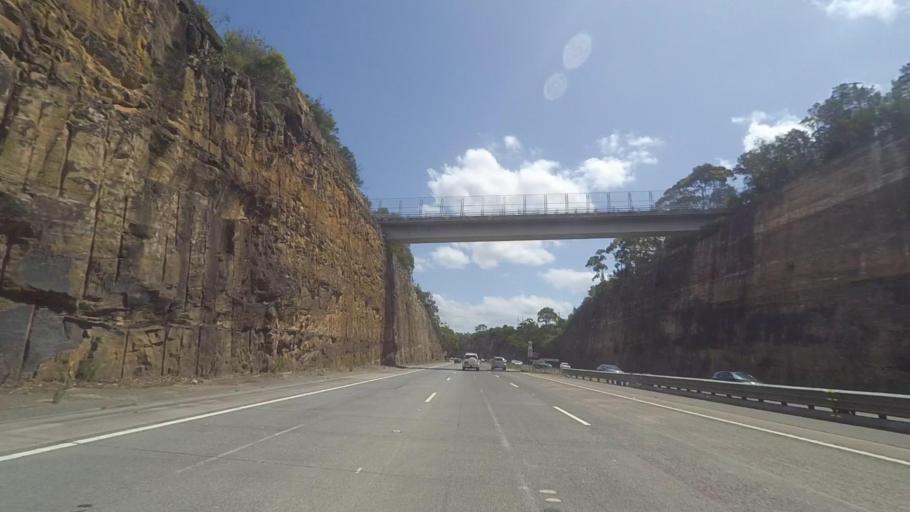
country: AU
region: New South Wales
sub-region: Hornsby Shire
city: Berowra
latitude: -33.6232
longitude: 151.1548
